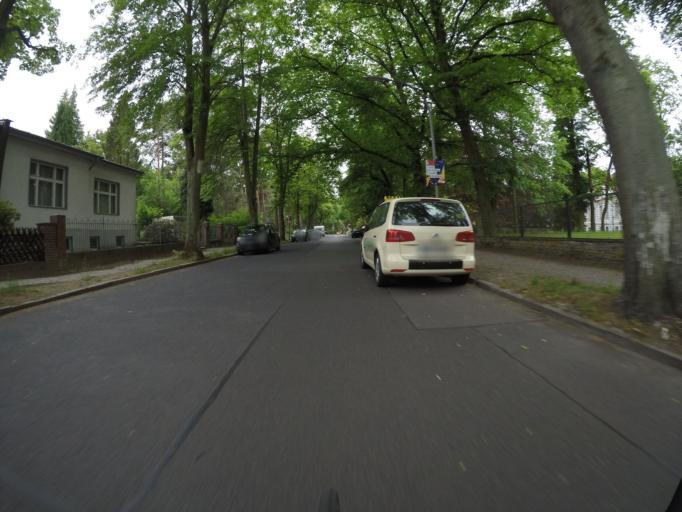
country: DE
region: Berlin
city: Waidmannslust
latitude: 52.6047
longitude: 13.3102
